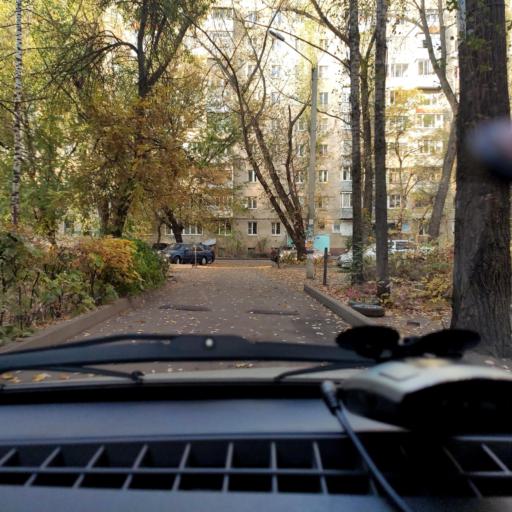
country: RU
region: Voronezj
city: Voronezh
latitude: 51.7023
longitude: 39.1912
